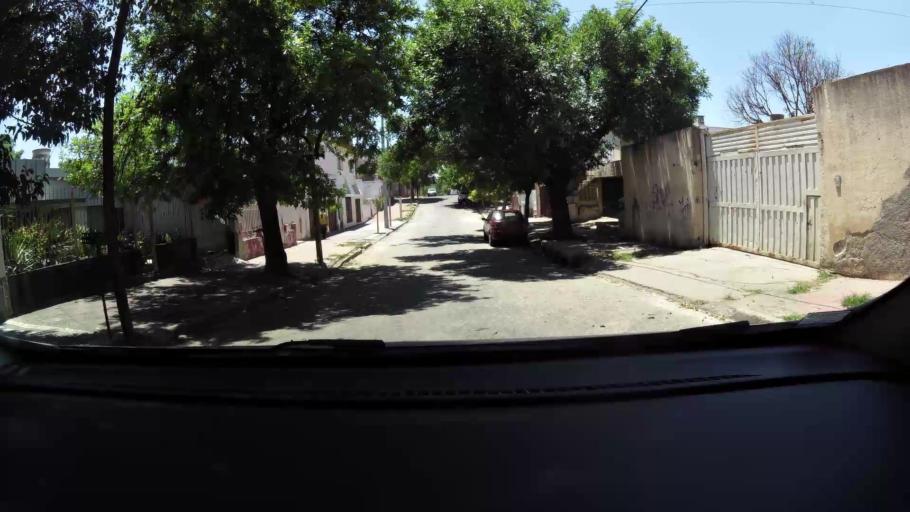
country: AR
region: Cordoba
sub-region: Departamento de Capital
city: Cordoba
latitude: -31.4023
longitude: -64.2154
